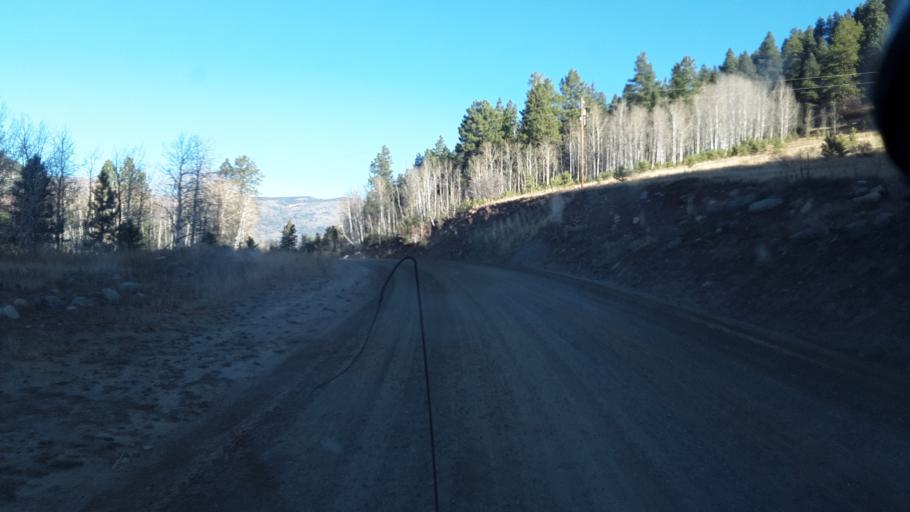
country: US
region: Colorado
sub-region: La Plata County
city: Bayfield
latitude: 37.3949
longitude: -107.6574
